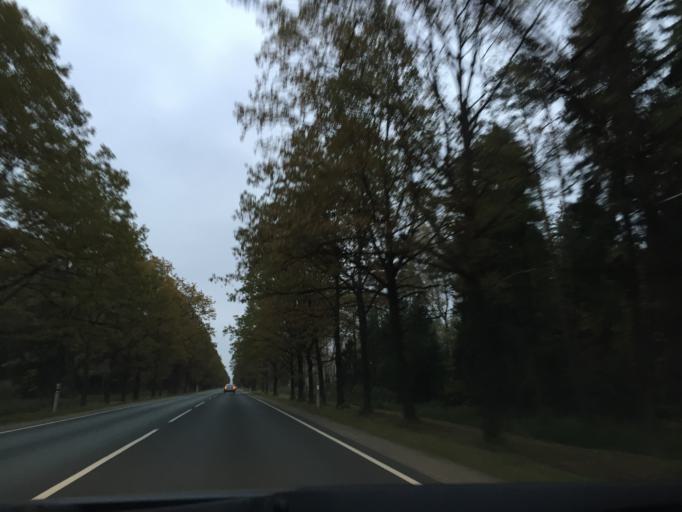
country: LV
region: Ozolnieku
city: Ozolnieki
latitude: 56.7012
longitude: 23.8126
